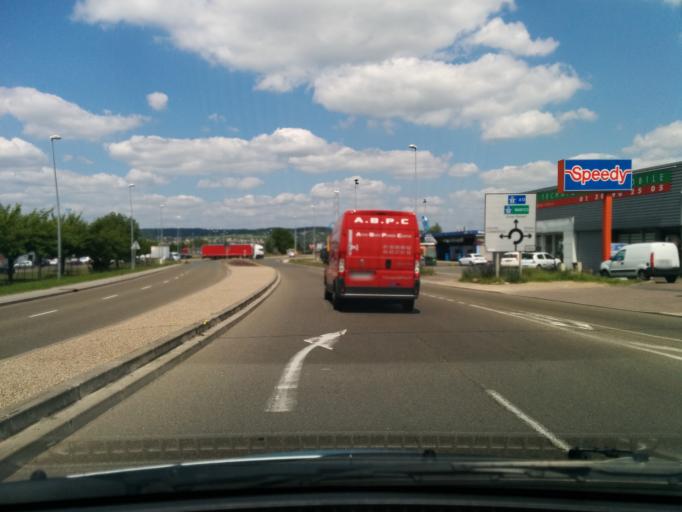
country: FR
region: Ile-de-France
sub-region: Departement des Yvelines
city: Flins-sur-Seine
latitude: 48.9652
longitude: 1.8659
